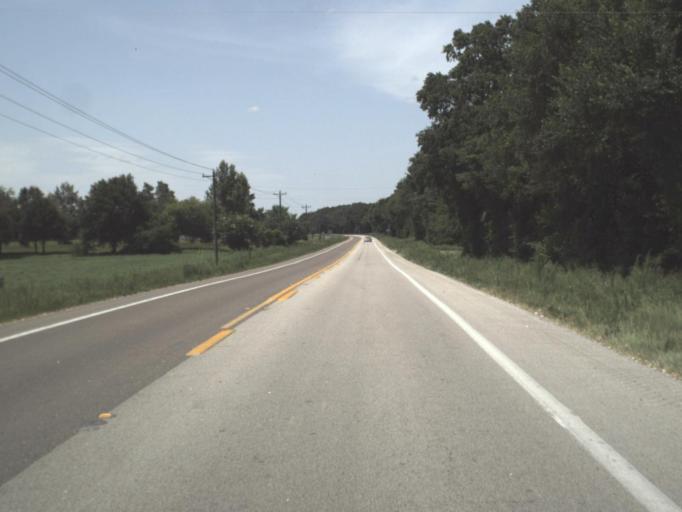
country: US
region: Florida
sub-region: Gilchrist County
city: Trenton
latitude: 29.7370
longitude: -82.8578
